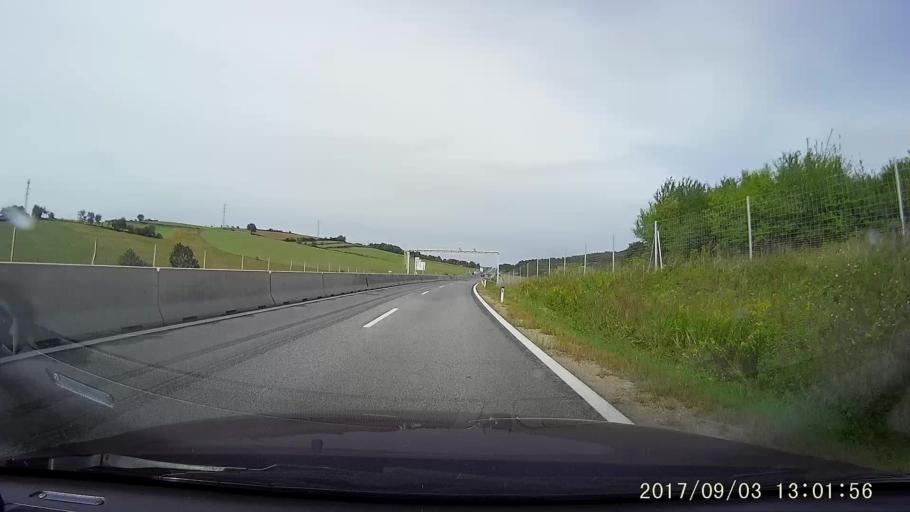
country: AT
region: Lower Austria
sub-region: Politischer Bezirk Hollabrunn
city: Hollabrunn
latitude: 48.5136
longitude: 16.0883
